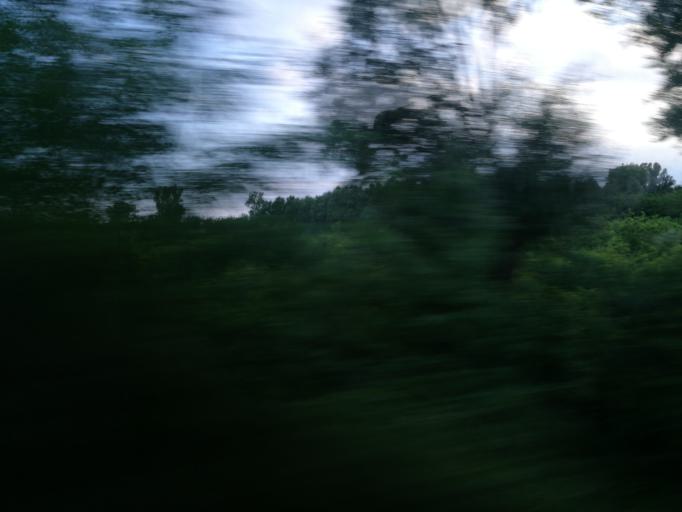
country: RO
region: Dambovita
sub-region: Comuna Contesti
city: Contesti
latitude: 44.6583
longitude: 25.6422
